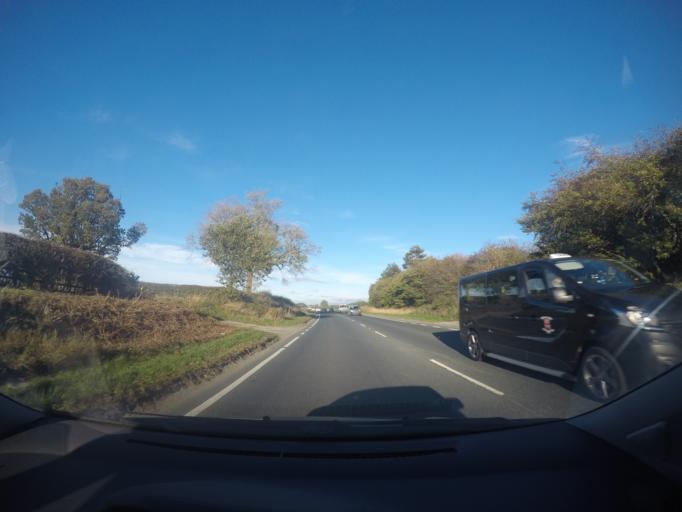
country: GB
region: England
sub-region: City of York
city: Copmanthorpe
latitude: 53.9254
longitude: -1.1461
